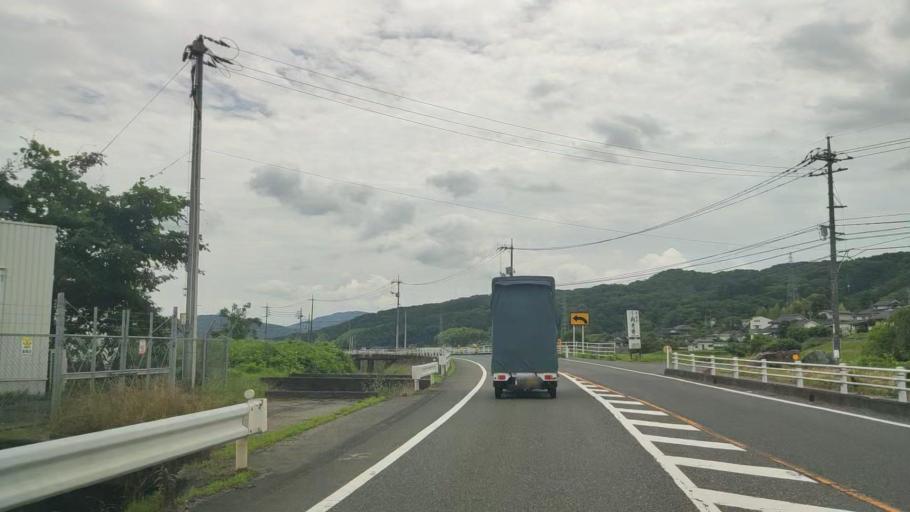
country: JP
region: Okayama
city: Tsuyama
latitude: 35.0557
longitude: 133.9096
